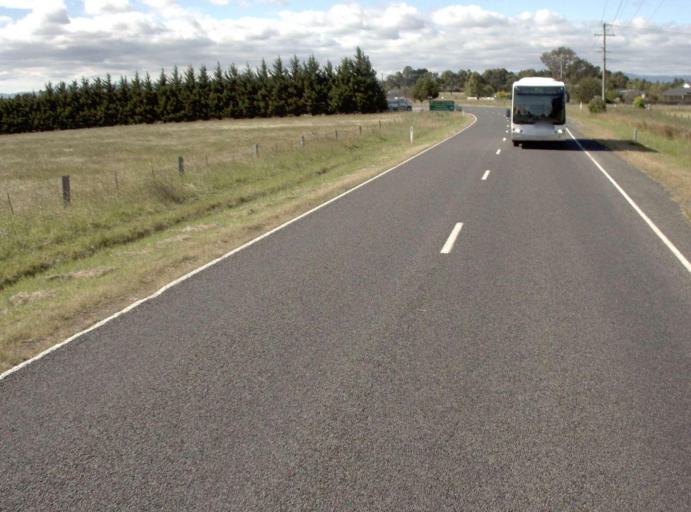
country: AU
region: Victoria
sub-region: Latrobe
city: Traralgon
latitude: -38.1804
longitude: 146.5002
